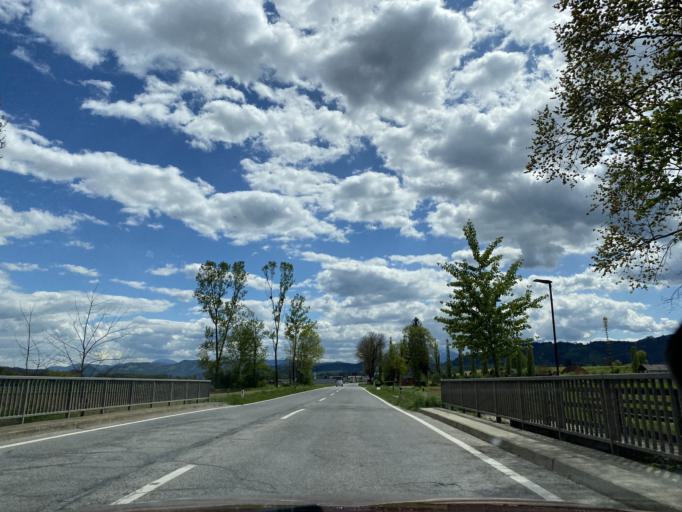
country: AT
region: Carinthia
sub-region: Politischer Bezirk Wolfsberg
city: Sankt Andrae
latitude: 46.7891
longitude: 14.8252
